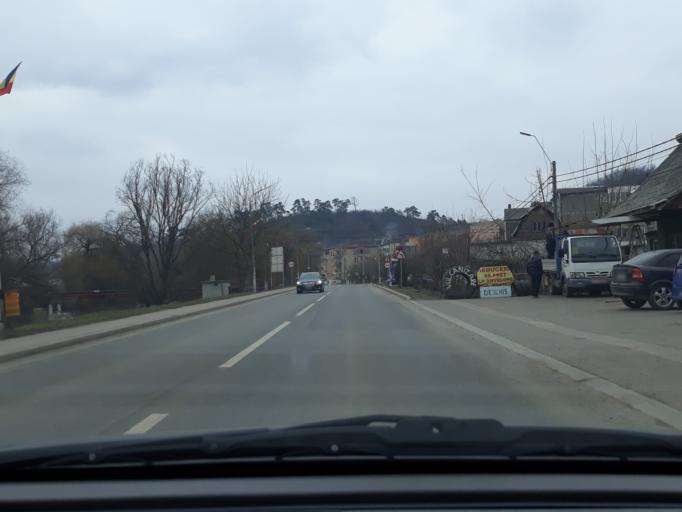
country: RO
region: Salaj
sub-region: Oras Simleu Silvaniei
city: Simleu Silvaniei
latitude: 47.2300
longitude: 22.7885
